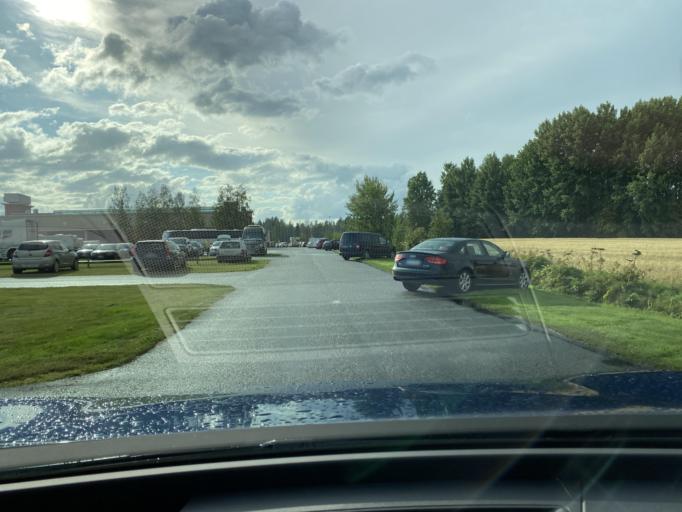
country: FI
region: Southern Ostrobothnia
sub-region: Seinaejoki
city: Alahaermae
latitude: 63.2306
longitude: 22.8476
